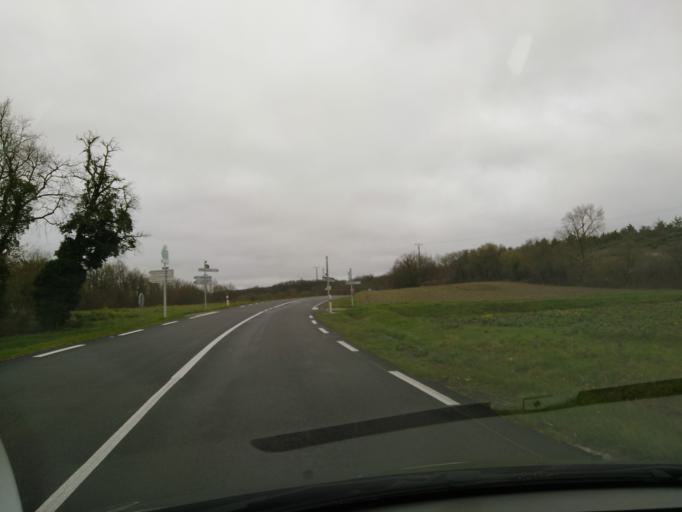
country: FR
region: Aquitaine
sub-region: Departement du Lot-et-Garonne
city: Castillonnes
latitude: 44.7261
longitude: 0.5487
